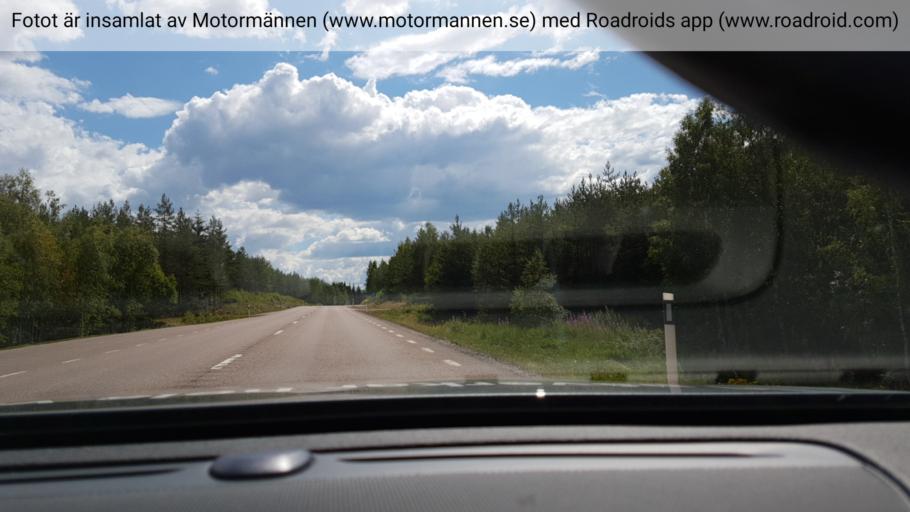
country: SE
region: Dalarna
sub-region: Faluns Kommun
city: Falun
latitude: 60.6485
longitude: 15.5656
